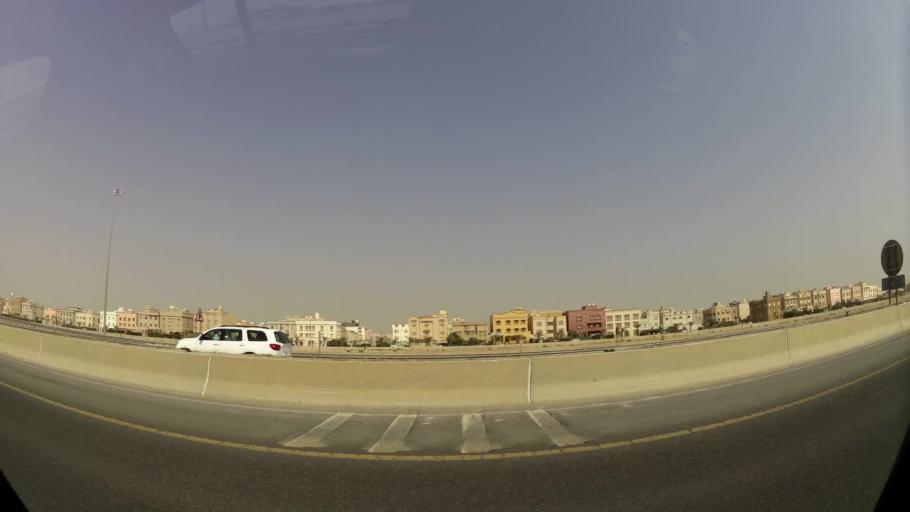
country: KW
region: Muhafazat al Jahra'
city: Al Jahra'
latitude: 29.3000
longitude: 47.6991
